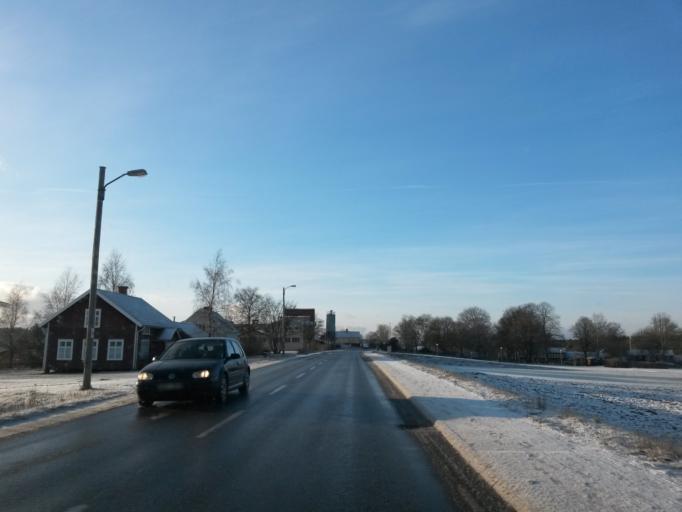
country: SE
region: Vaestra Goetaland
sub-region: Alingsas Kommun
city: Sollebrunn
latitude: 58.1135
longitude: 12.6267
